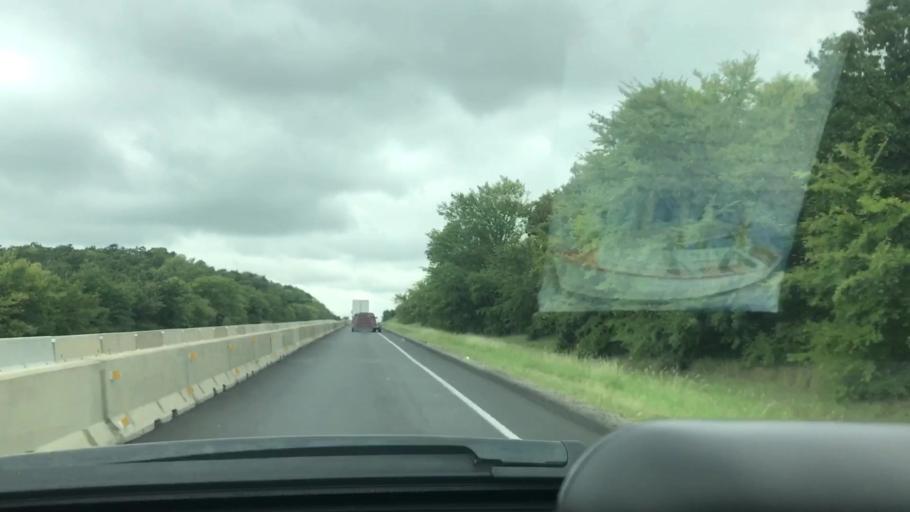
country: US
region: Oklahoma
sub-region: McIntosh County
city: Eufaula
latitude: 35.2684
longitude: -95.5912
